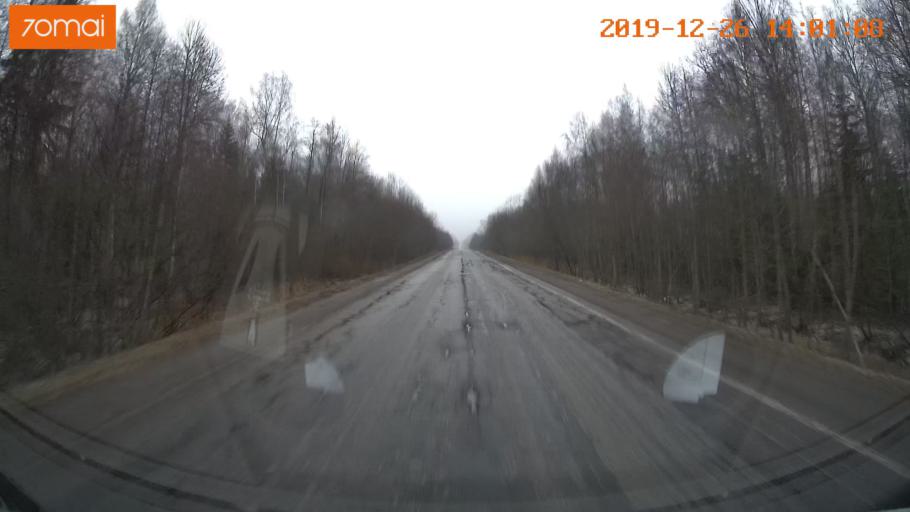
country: RU
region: Jaroslavl
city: Poshekhon'ye
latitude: 58.5527
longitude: 38.7580
